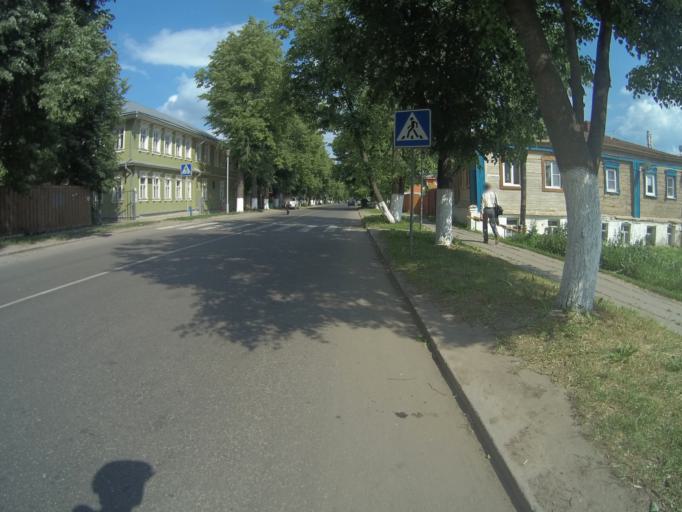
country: RU
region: Vladimir
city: Suzdal'
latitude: 56.4199
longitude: 40.4527
